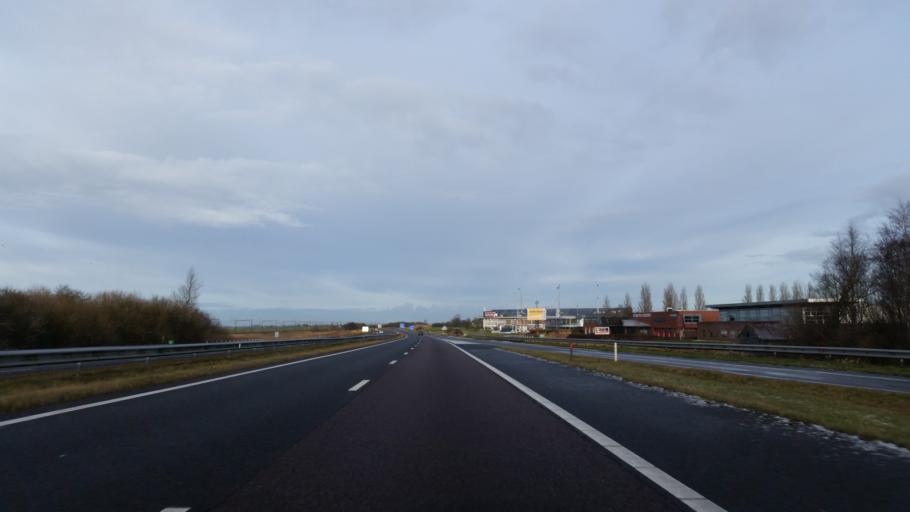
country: NL
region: Friesland
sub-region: Gemeente Boarnsterhim
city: Grou
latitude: 53.0930
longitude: 5.8227
